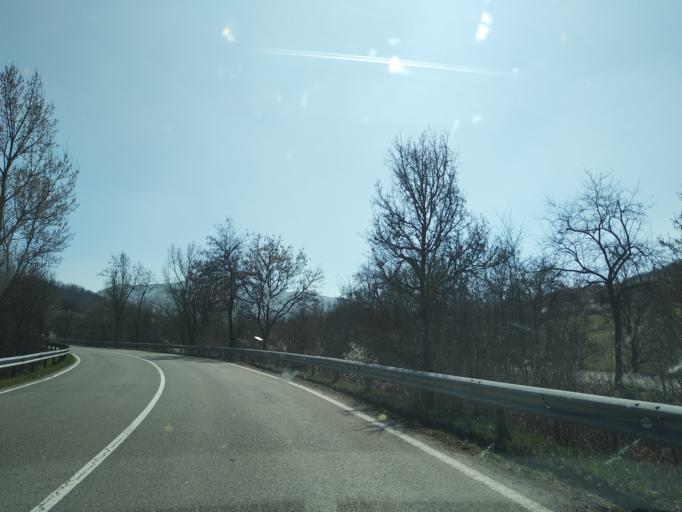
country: IT
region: Emilia-Romagna
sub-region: Provincia di Reggio Emilia
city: Vezzano sul Crostolo
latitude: 44.5771
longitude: 10.5278
